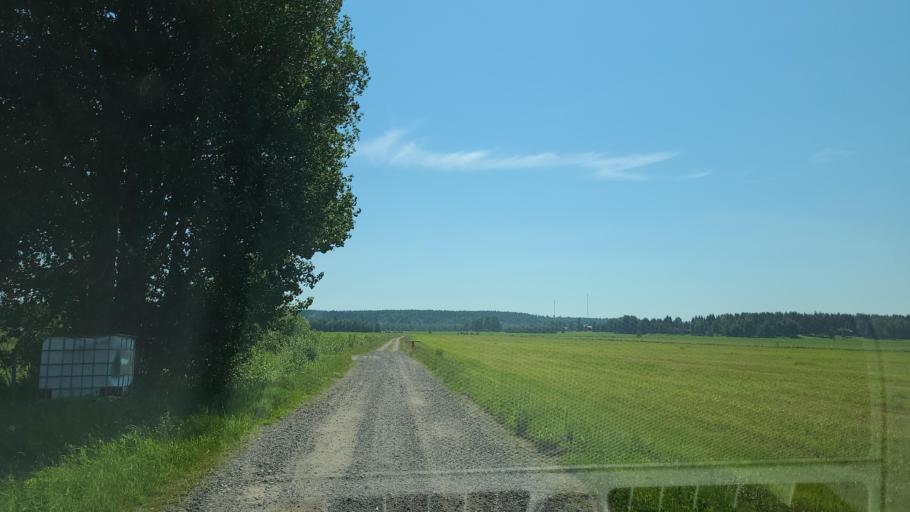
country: SE
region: Vaesterbotten
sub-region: Robertsfors Kommun
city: Robertsfors
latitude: 64.0868
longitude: 20.8522
